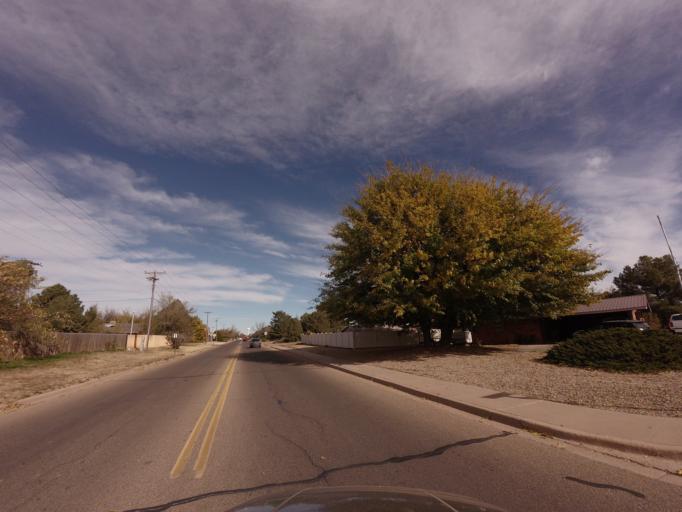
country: US
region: New Mexico
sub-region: Curry County
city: Clovis
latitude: 34.4153
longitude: -103.1877
